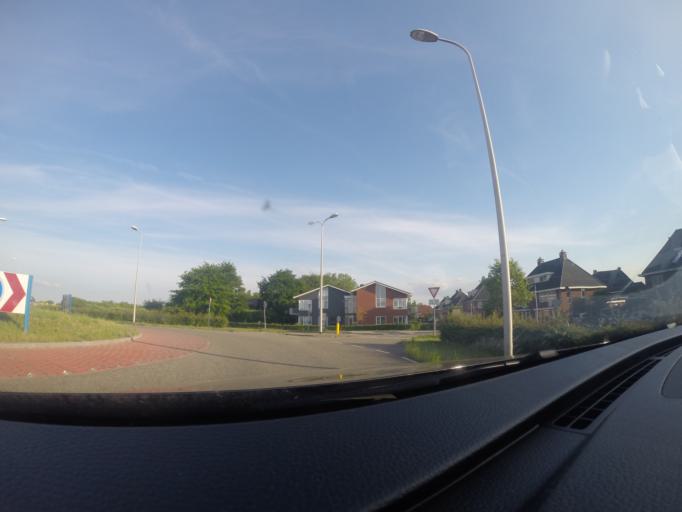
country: NL
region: Overijssel
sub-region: Gemeente Kampen
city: Kampen
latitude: 52.5378
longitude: 5.9363
